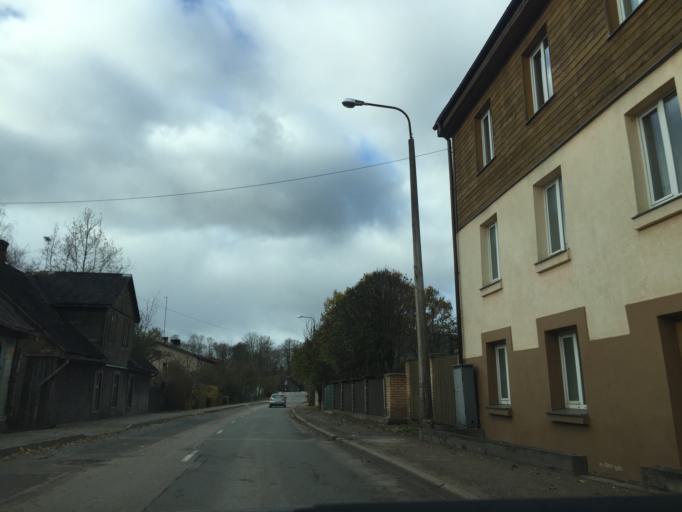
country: LV
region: Tukuma Rajons
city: Tukums
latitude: 56.9678
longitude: 23.1441
